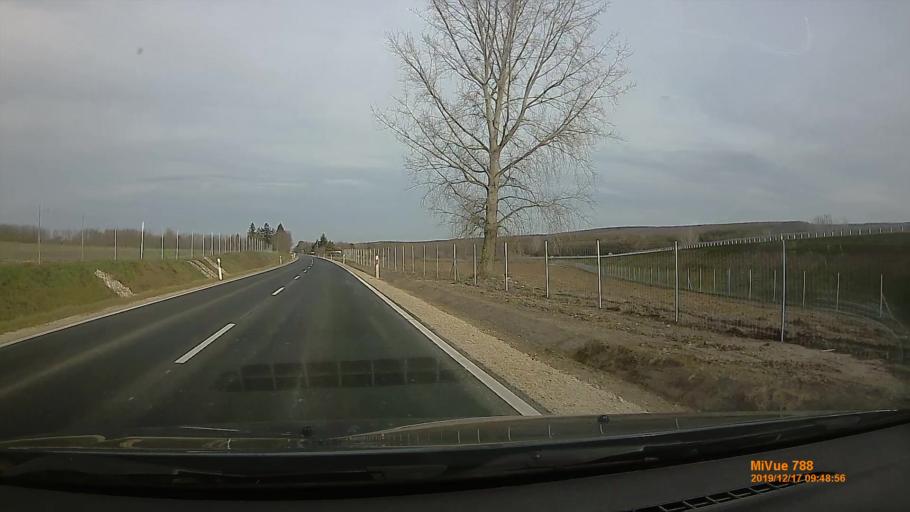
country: HU
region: Somogy
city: Karad
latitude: 46.5956
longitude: 17.8011
